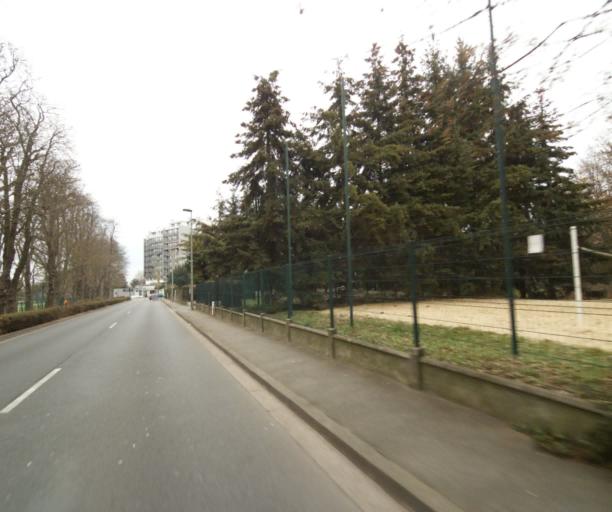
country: FR
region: Ile-de-France
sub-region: Departement des Hauts-de-Seine
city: Saint-Cloud
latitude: 48.8560
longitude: 2.2087
